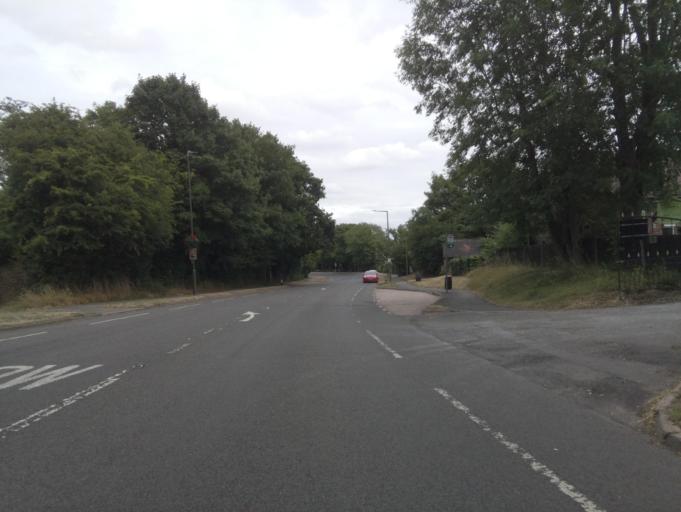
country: GB
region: England
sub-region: Derbyshire
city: Long Eaton
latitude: 52.9167
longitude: -1.3218
